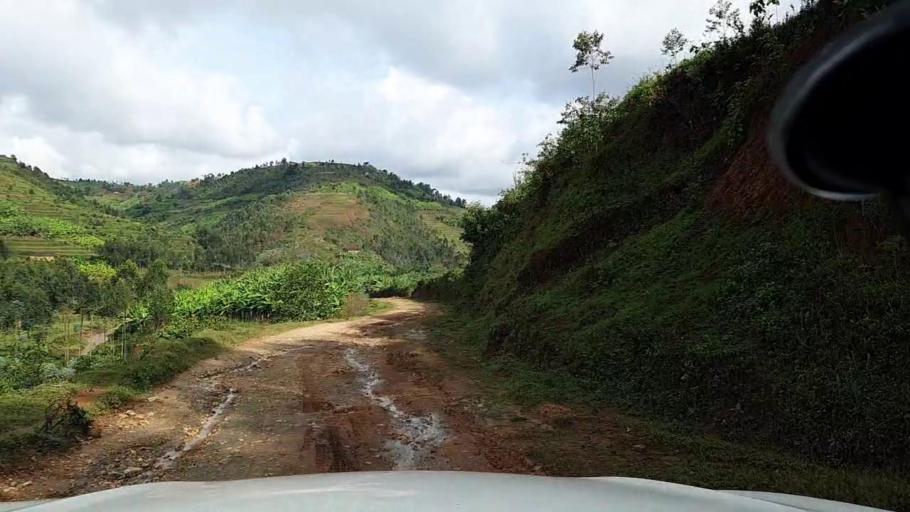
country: RW
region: Western Province
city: Kibuye
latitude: -2.1335
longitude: 29.5023
